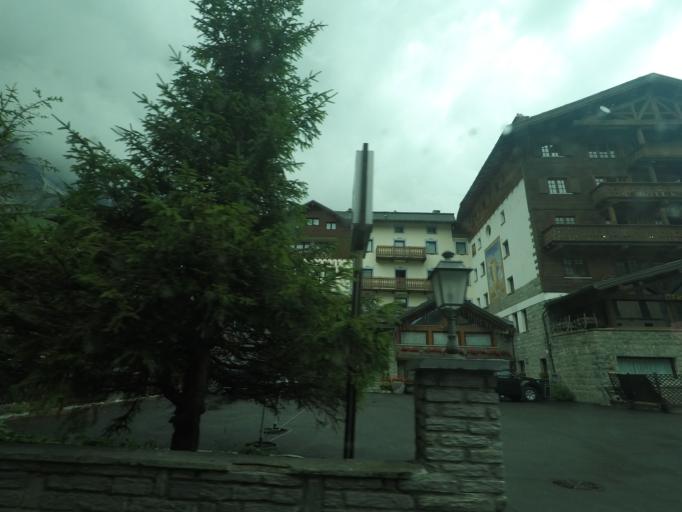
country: IT
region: Aosta Valley
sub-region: Valle d'Aosta
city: Paquier
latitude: 45.9370
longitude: 7.6292
